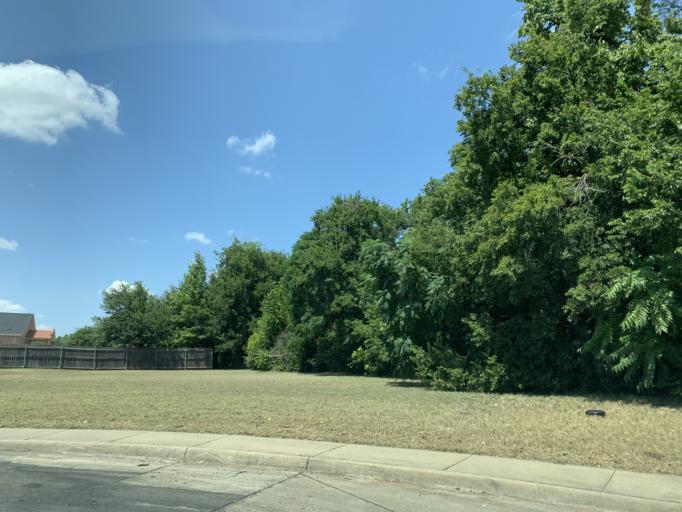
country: US
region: Texas
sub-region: Dallas County
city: Hutchins
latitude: 32.6846
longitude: -96.7824
